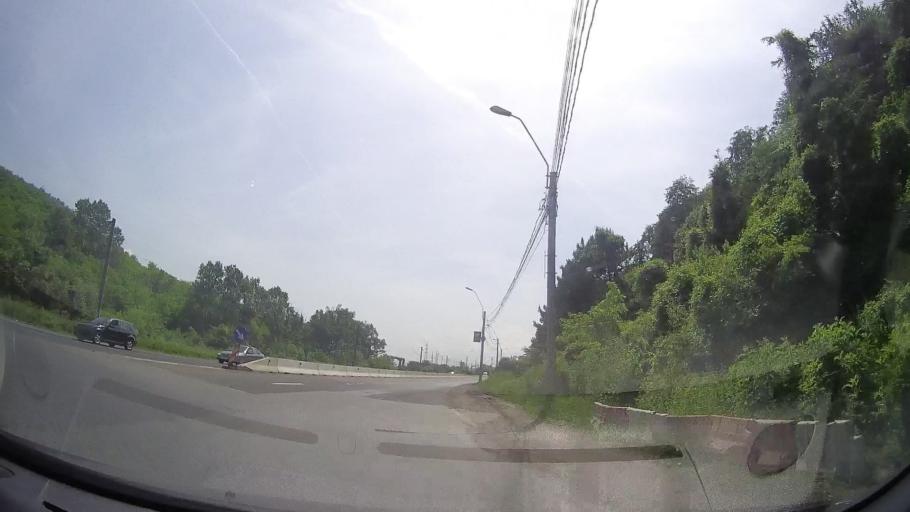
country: RO
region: Hunedoara
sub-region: Comuna Soimus
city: Soimus
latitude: 45.9026
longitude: 22.8839
